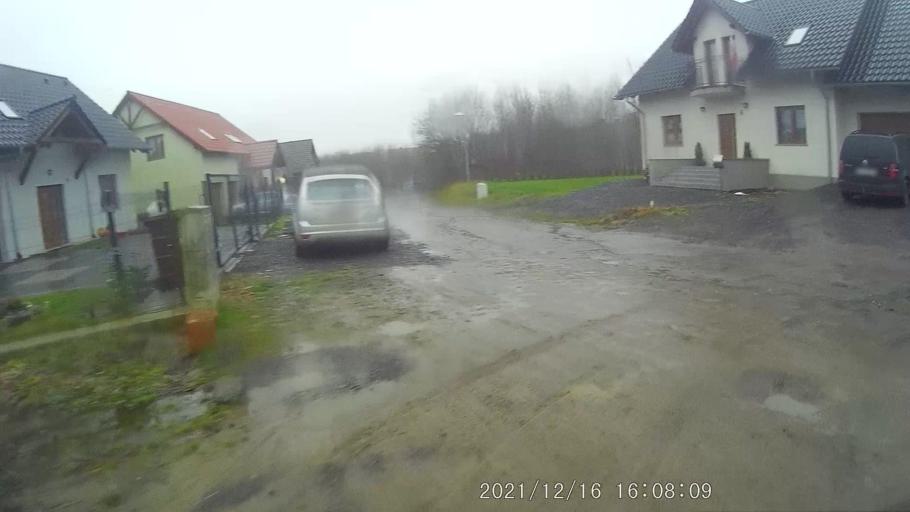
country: PL
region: Lower Silesian Voivodeship
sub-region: Powiat zgorzelecki
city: Lagow
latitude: 51.1585
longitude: 15.0494
